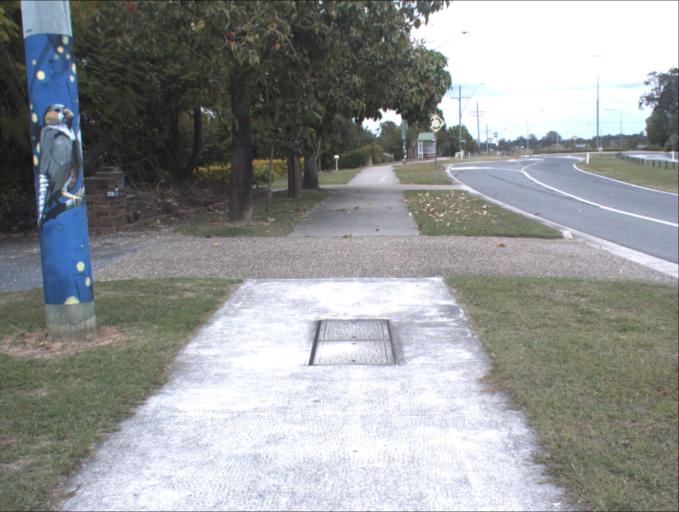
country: AU
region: Queensland
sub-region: Logan
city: Logan Reserve
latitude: -27.6811
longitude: 153.0607
